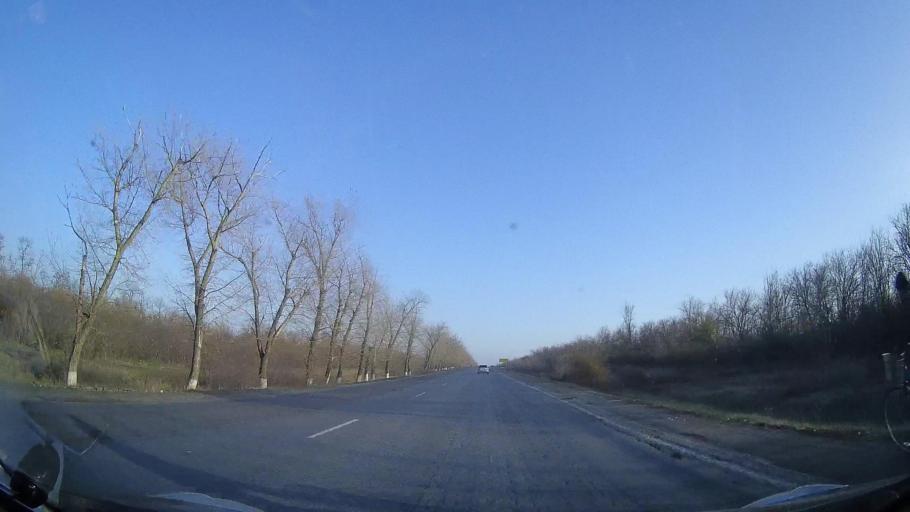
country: RU
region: Rostov
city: Bataysk
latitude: 47.0786
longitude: 39.7792
